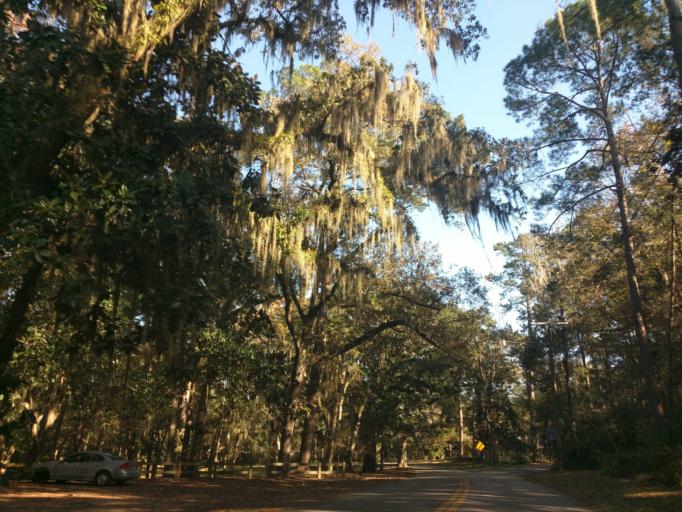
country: US
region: Florida
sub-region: Leon County
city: Tallahassee
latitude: 30.4316
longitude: -84.2720
